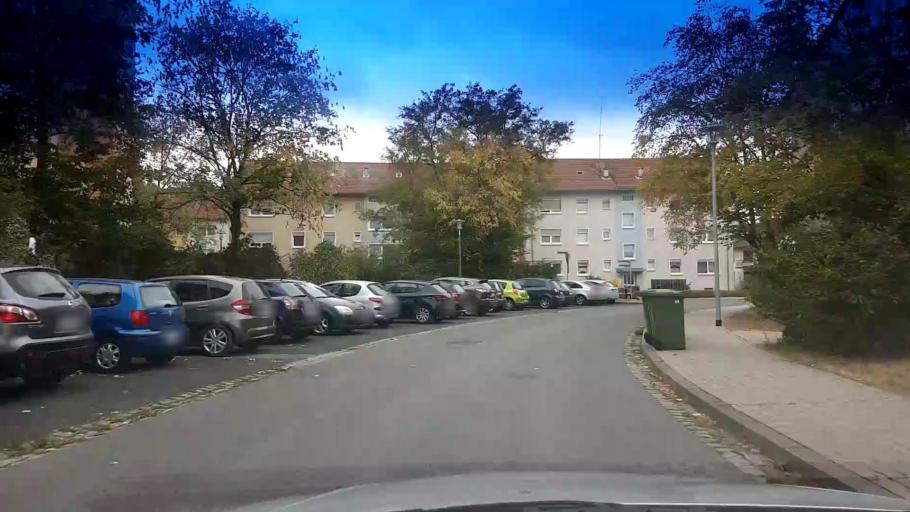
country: DE
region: Bavaria
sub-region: Upper Franconia
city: Hallstadt
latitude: 49.9241
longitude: 10.8808
